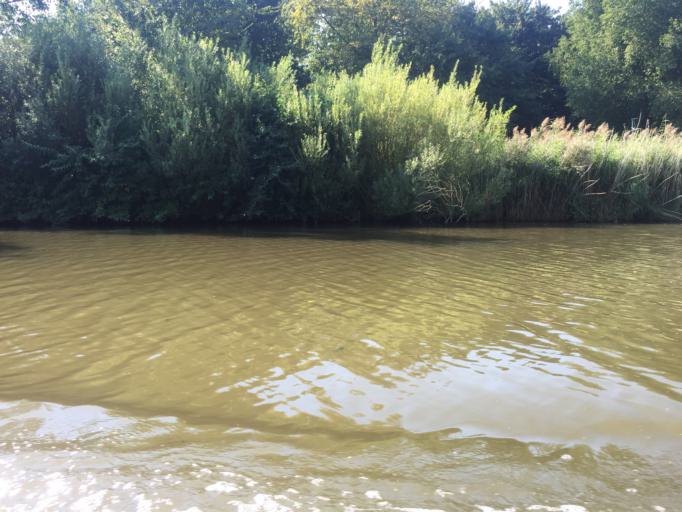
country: NL
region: Flevoland
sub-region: Gemeente Almere
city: Almere Stad
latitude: 52.3801
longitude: 5.1928
